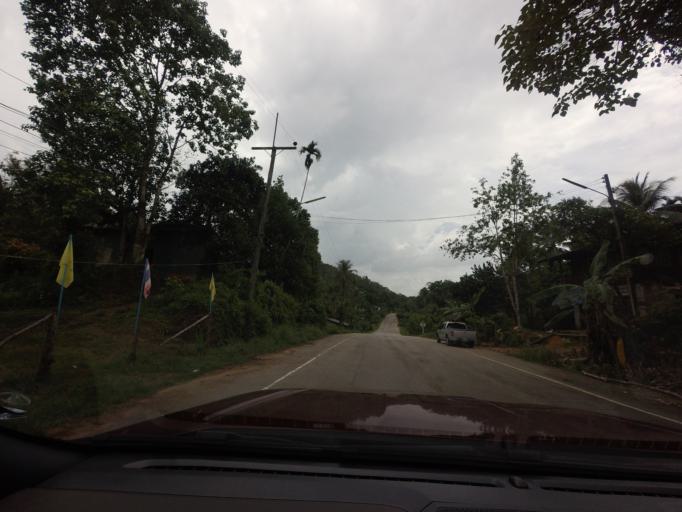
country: TH
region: Narathiwat
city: Sukhirin
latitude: 5.9820
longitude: 101.6917
